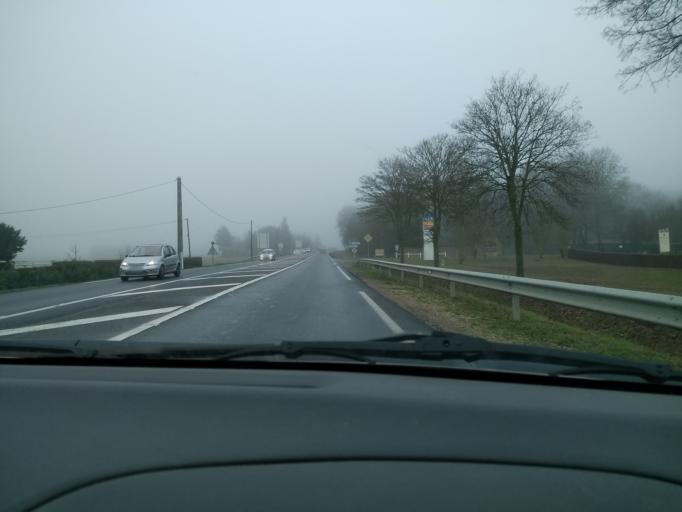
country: FR
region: Centre
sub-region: Departement d'Eure-et-Loir
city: Chateaudun
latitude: 48.0967
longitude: 1.3308
